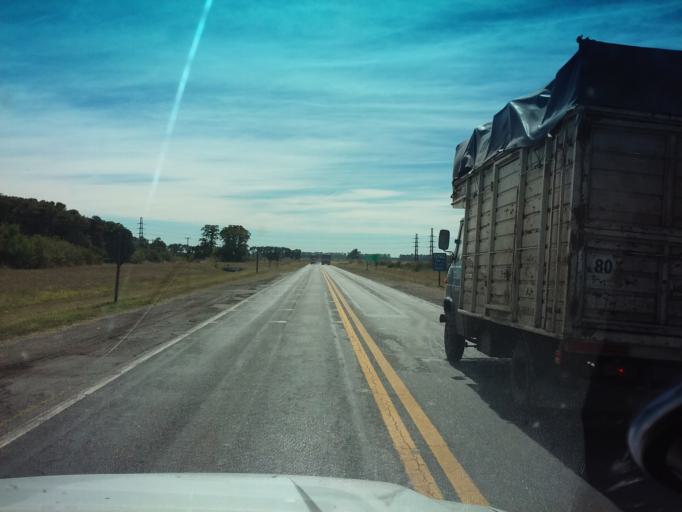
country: AR
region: Buenos Aires
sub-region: Partido de Bragado
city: Bragado
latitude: -35.1222
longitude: -60.4359
